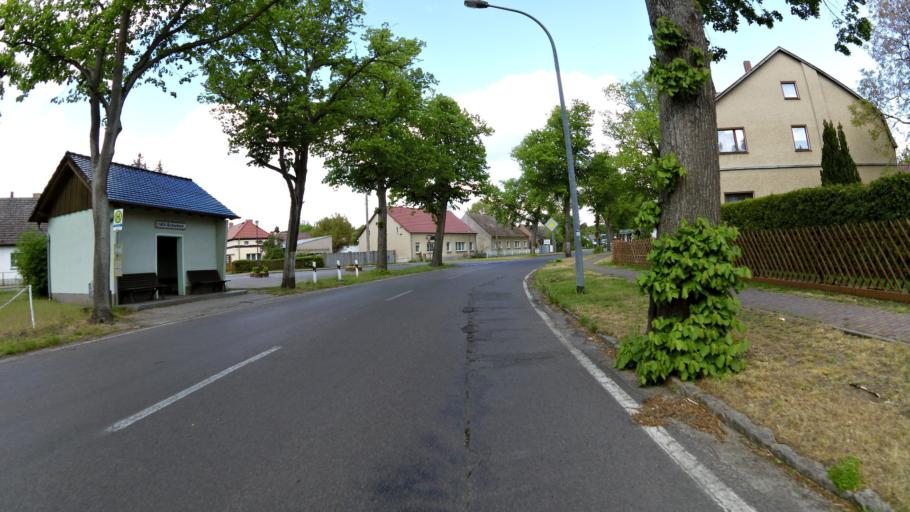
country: DE
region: Brandenburg
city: Schlepzig
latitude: 52.1206
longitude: 13.9496
